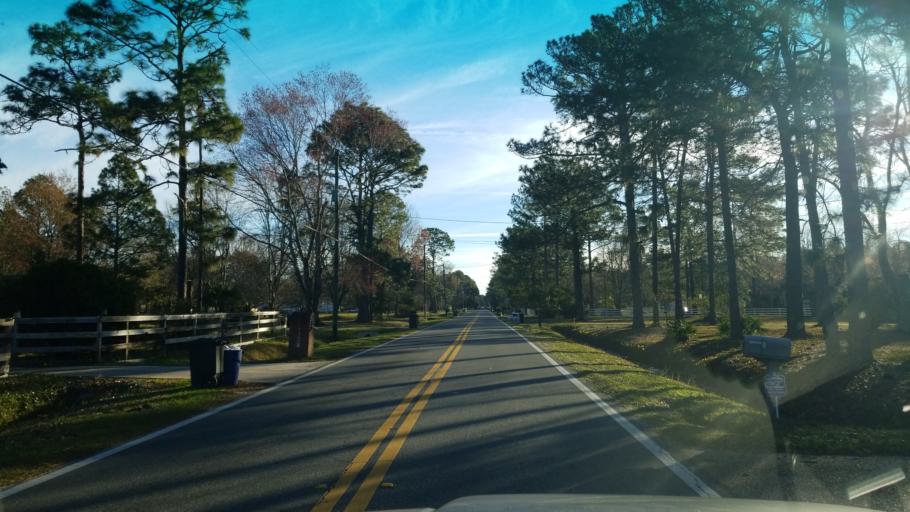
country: US
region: Florida
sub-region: Duval County
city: Baldwin
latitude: 30.3326
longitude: -81.8483
